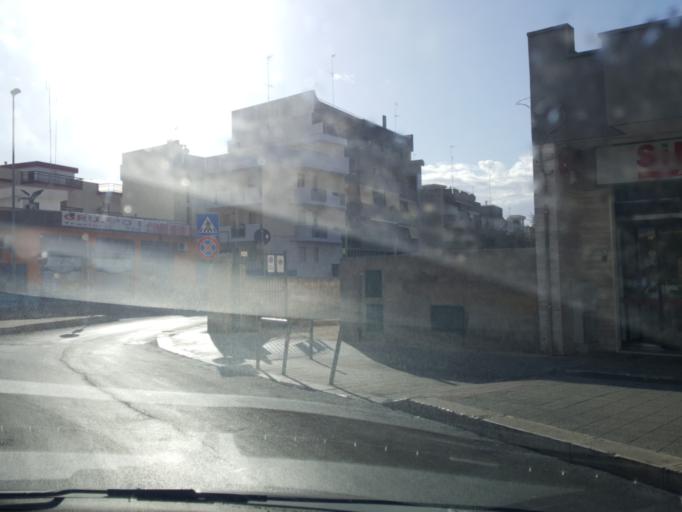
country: IT
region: Apulia
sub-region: Provincia di Bari
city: Triggiano
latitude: 41.0671
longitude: 16.9321
